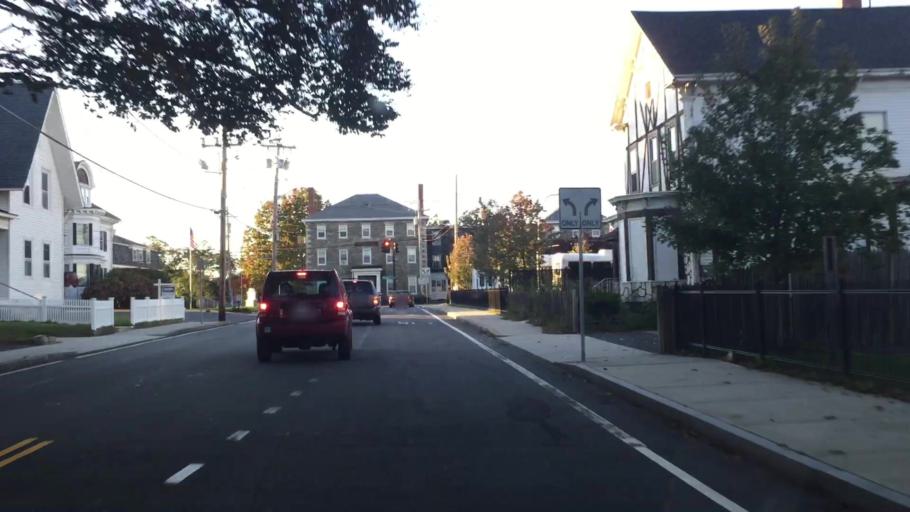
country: US
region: Massachusetts
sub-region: Middlesex County
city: Lowell
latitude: 42.6490
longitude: -71.3249
